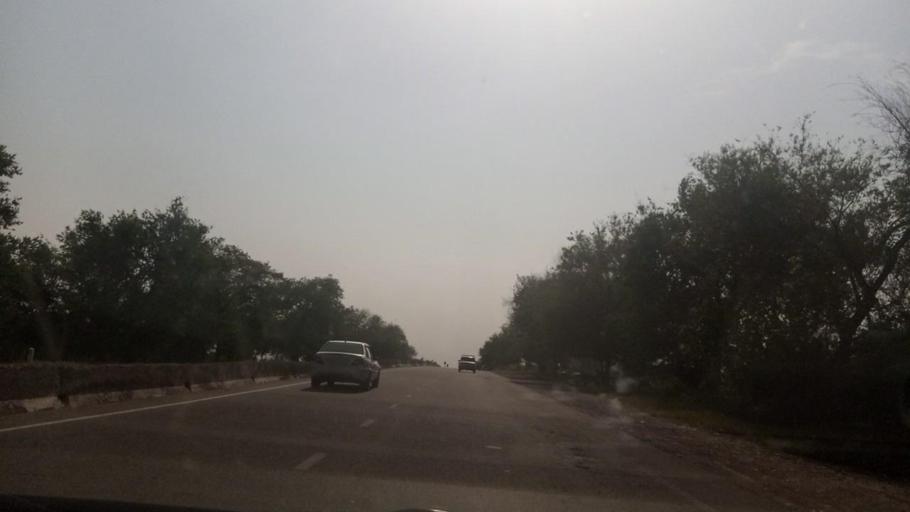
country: UZ
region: Toshkent
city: Angren
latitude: 40.9580
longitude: 69.9362
